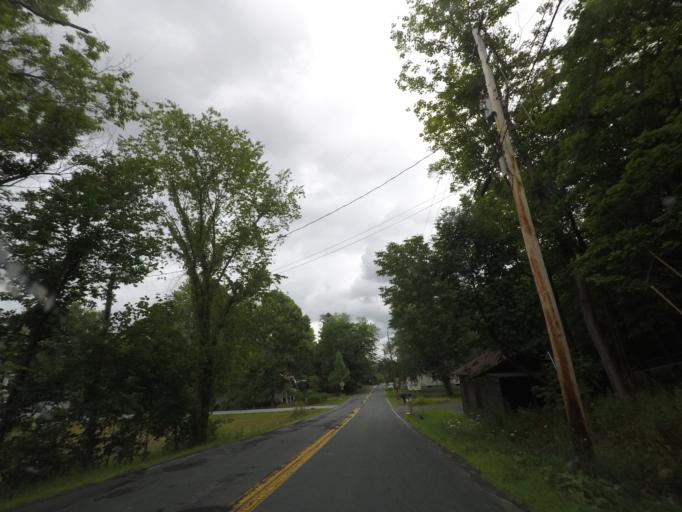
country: US
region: New York
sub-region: Rensselaer County
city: Wynantskill
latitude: 42.6817
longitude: -73.6344
